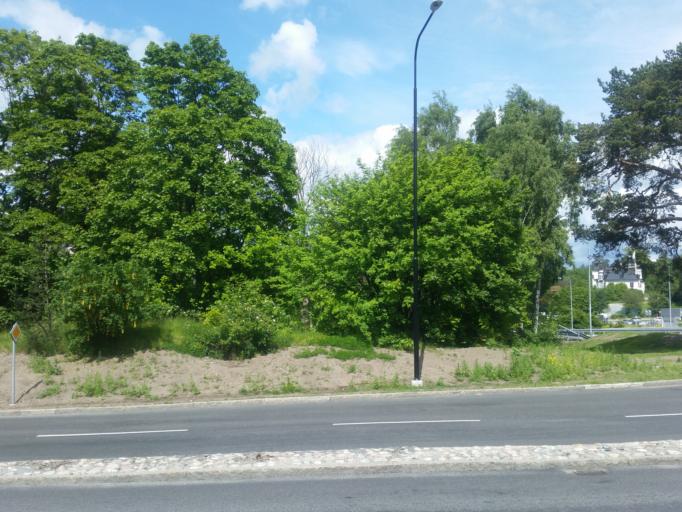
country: SE
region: Stockholm
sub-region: Solna Kommun
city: Solna
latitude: 59.3638
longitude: 18.0153
